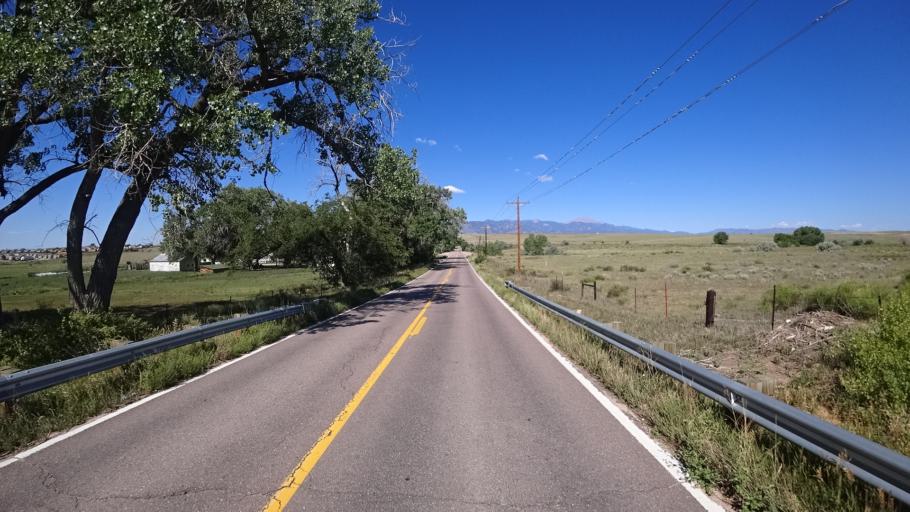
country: US
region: Colorado
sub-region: El Paso County
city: Security-Widefield
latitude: 38.7382
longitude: -104.6634
